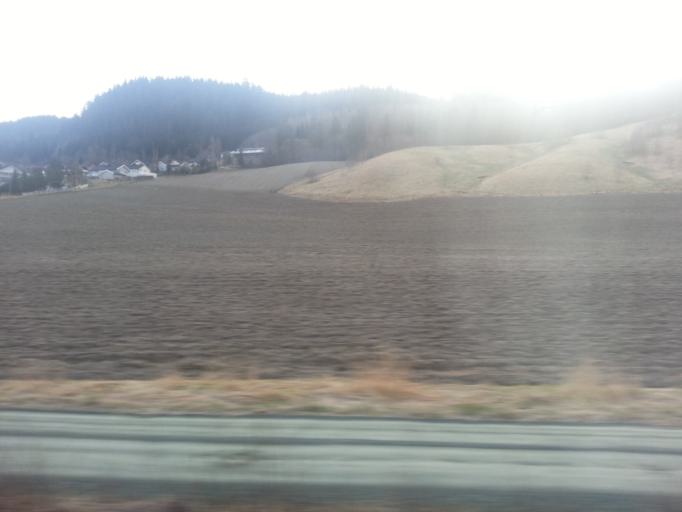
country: NO
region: Sor-Trondelag
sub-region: Melhus
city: Melhus
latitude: 63.2308
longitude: 10.2833
